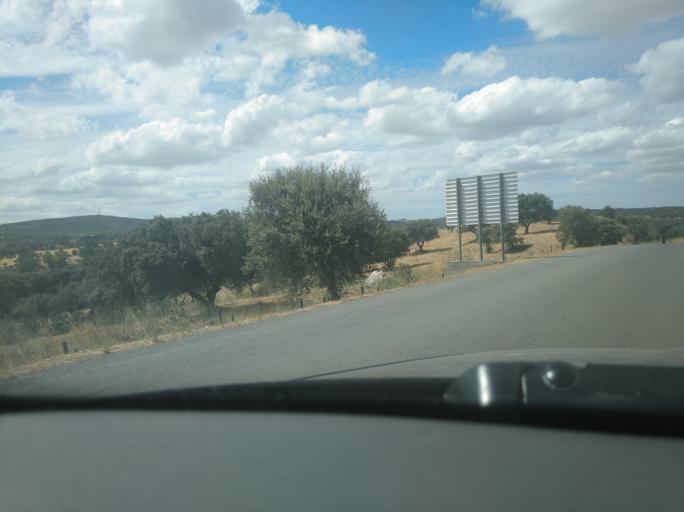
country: PT
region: Portalegre
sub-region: Arronches
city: Arronches
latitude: 39.0599
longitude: -7.4365
